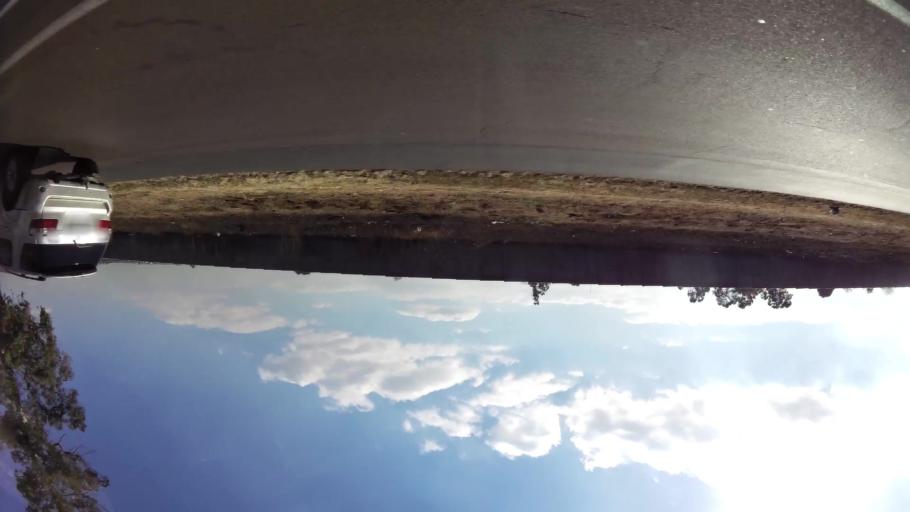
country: ZA
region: Gauteng
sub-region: City of Johannesburg Metropolitan Municipality
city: Soweto
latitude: -26.2819
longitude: 27.9084
